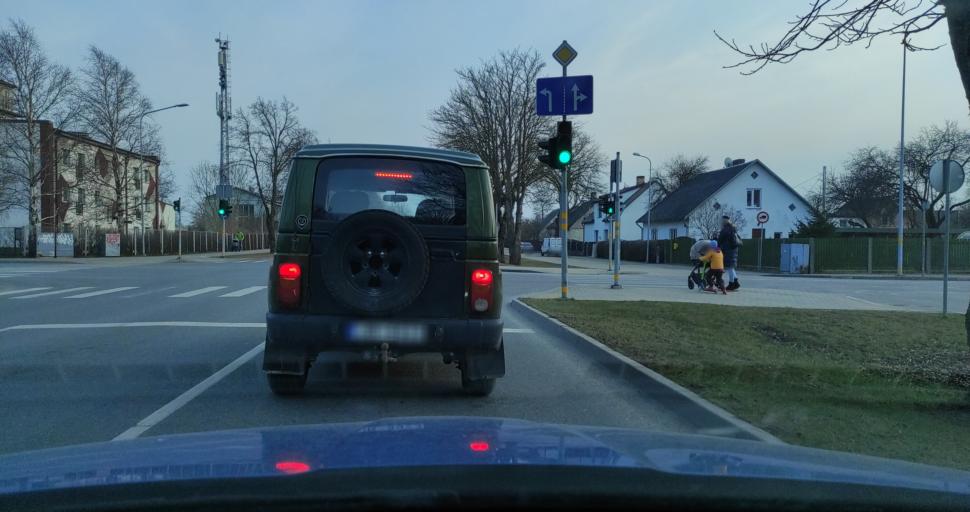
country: LV
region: Ventspils
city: Ventspils
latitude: 57.3822
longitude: 21.5664
